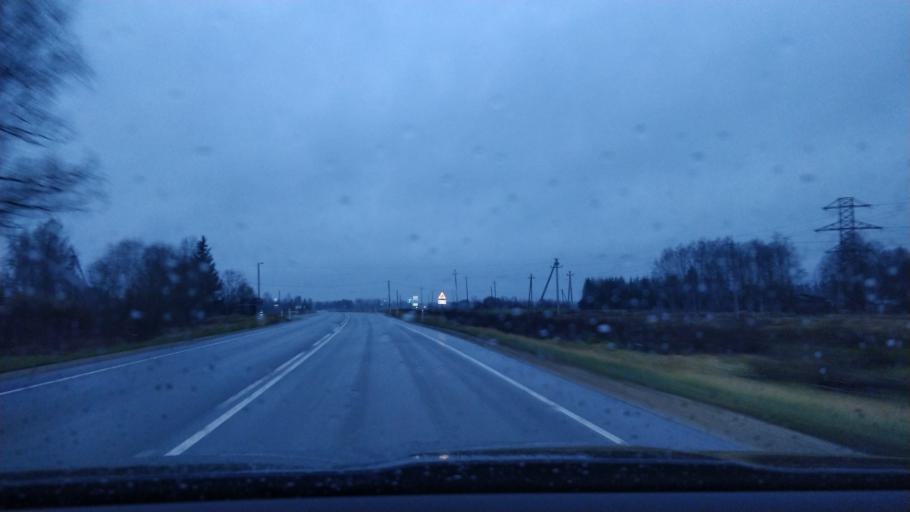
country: EE
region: Harju
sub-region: Nissi vald
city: Turba
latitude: 58.8852
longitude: 24.0899
